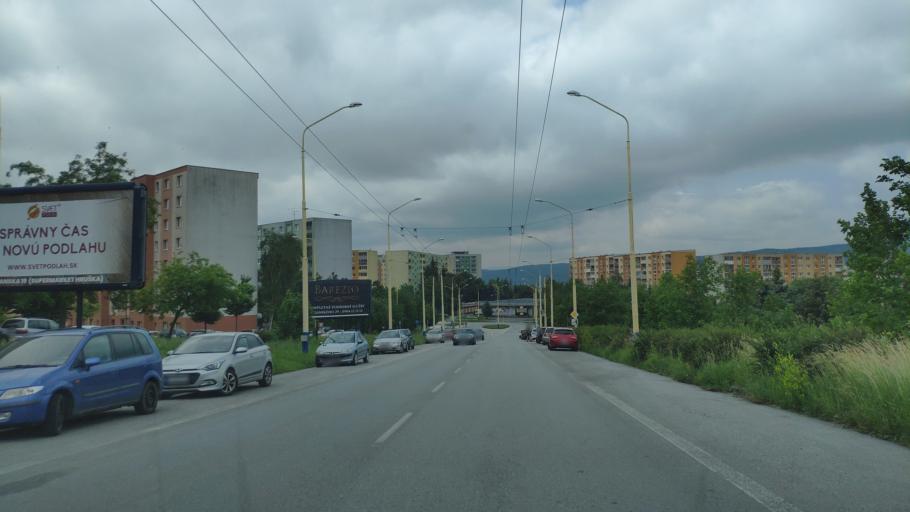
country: SK
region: Presovsky
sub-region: Okres Presov
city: Presov
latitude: 48.9909
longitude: 21.2700
